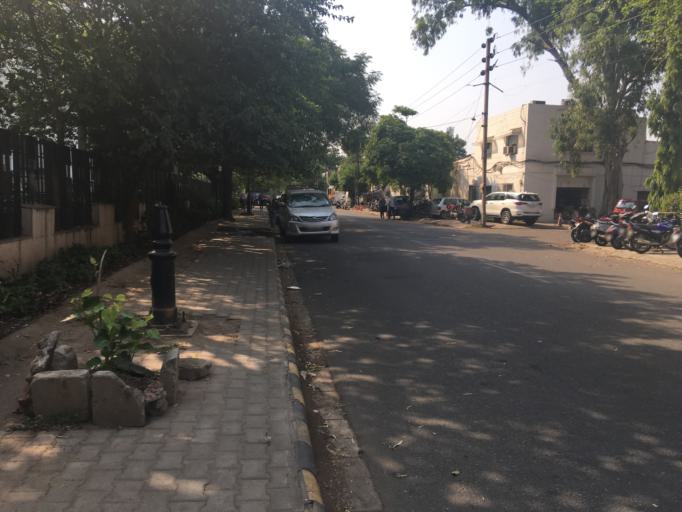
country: IN
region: Chandigarh
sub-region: Chandigarh
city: Chandigarh
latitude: 30.7056
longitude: 76.8023
